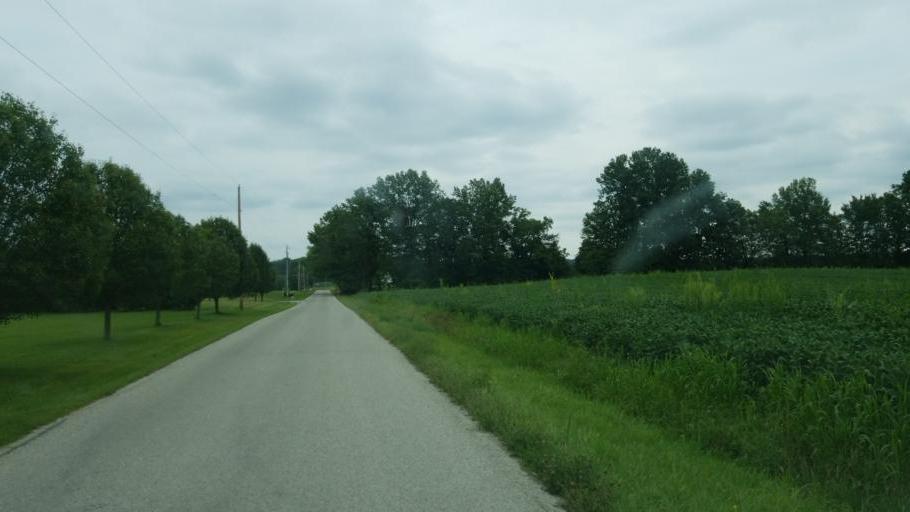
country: US
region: Ohio
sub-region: Morrow County
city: Mount Gilead
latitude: 40.5266
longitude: -82.8084
